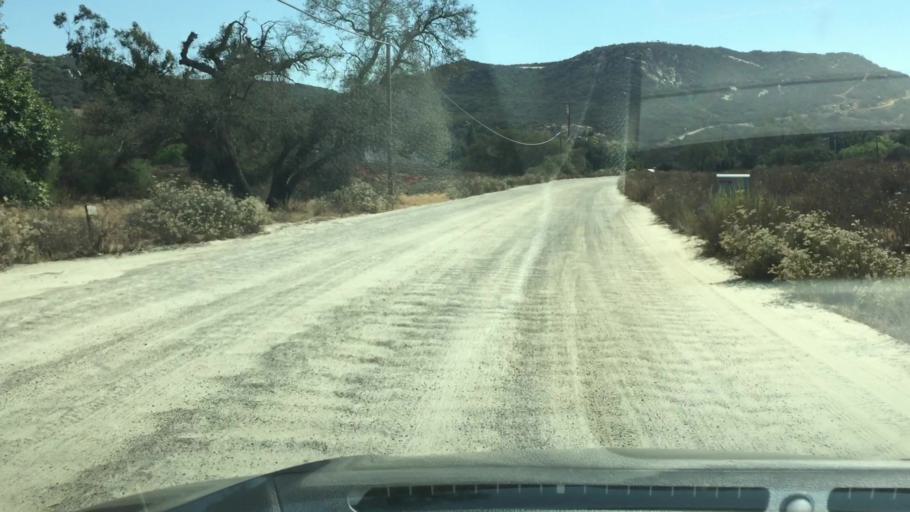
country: US
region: California
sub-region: San Diego County
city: Alpine
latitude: 32.7528
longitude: -116.7575
